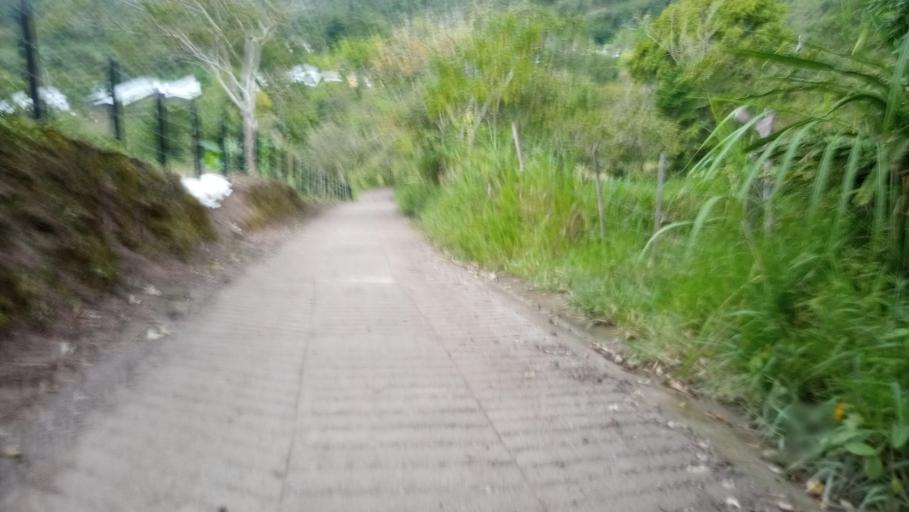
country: CO
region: Cundinamarca
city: Tenza
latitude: 5.0861
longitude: -73.4215
